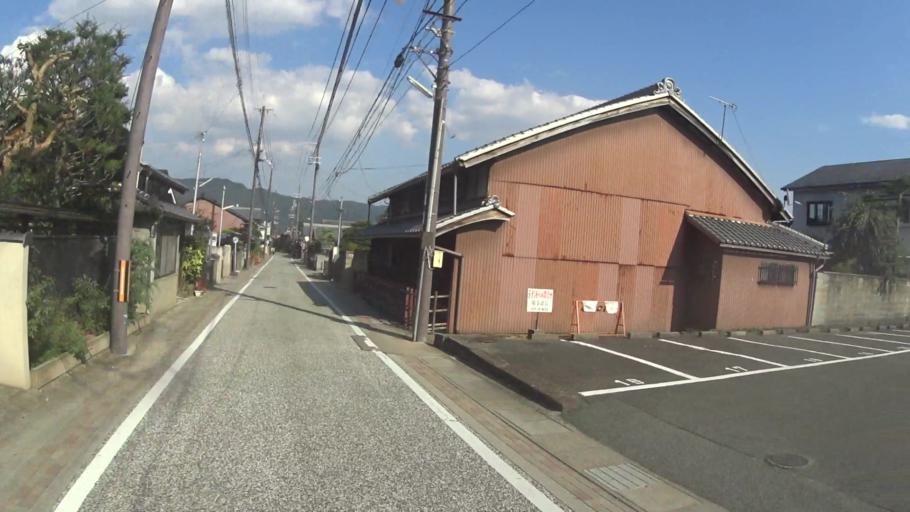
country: JP
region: Kyoto
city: Kameoka
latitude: 35.0085
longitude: 135.5843
